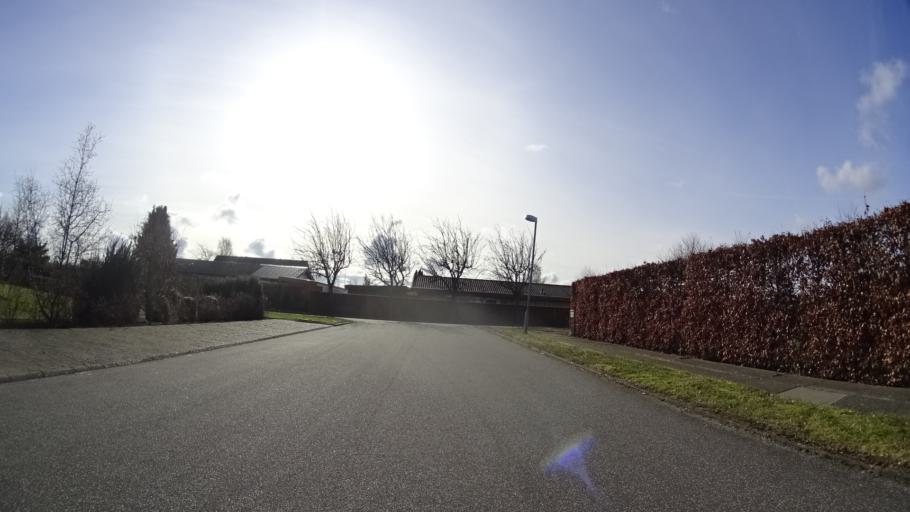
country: DK
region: Central Jutland
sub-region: Arhus Kommune
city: Tranbjerg
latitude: 56.0907
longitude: 10.1262
